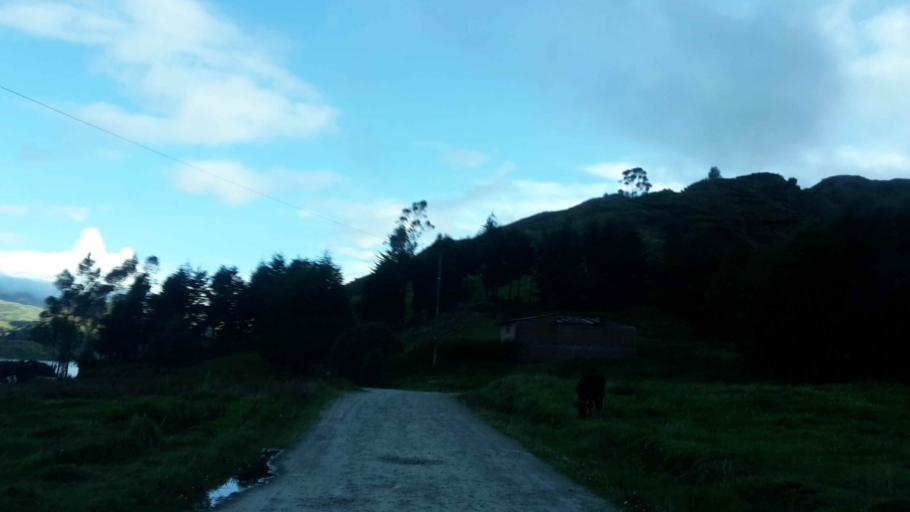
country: BO
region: Cochabamba
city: Colomi
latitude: -17.2481
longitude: -65.9068
